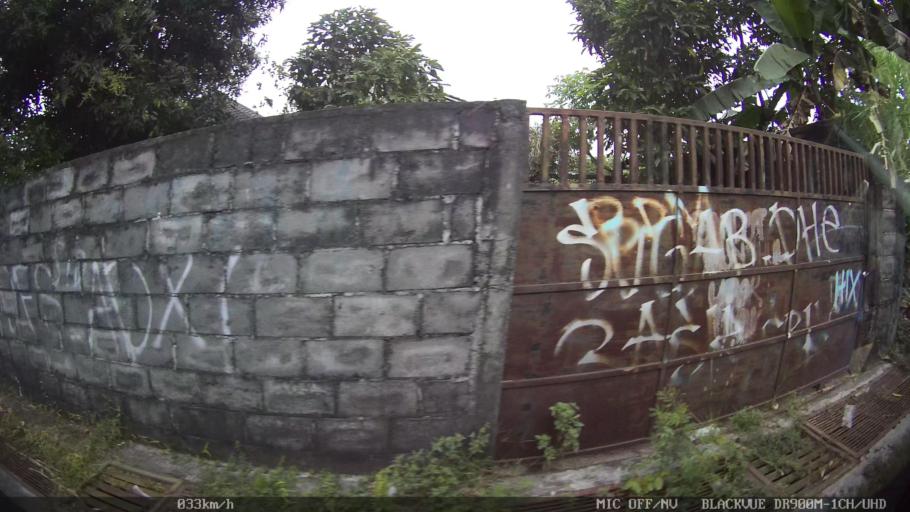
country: ID
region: Daerah Istimewa Yogyakarta
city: Gamping Lor
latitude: -7.7757
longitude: 110.3370
